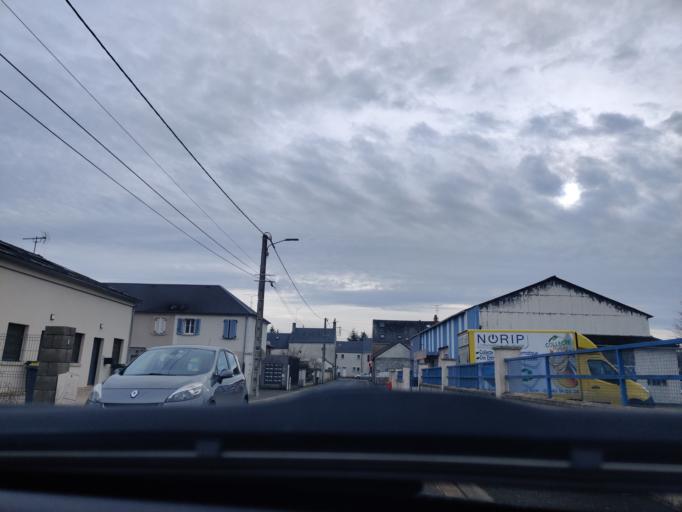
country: FR
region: Centre
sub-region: Departement du Loiret
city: La Chapelle-Saint-Mesmin
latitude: 47.8884
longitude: 1.8307
